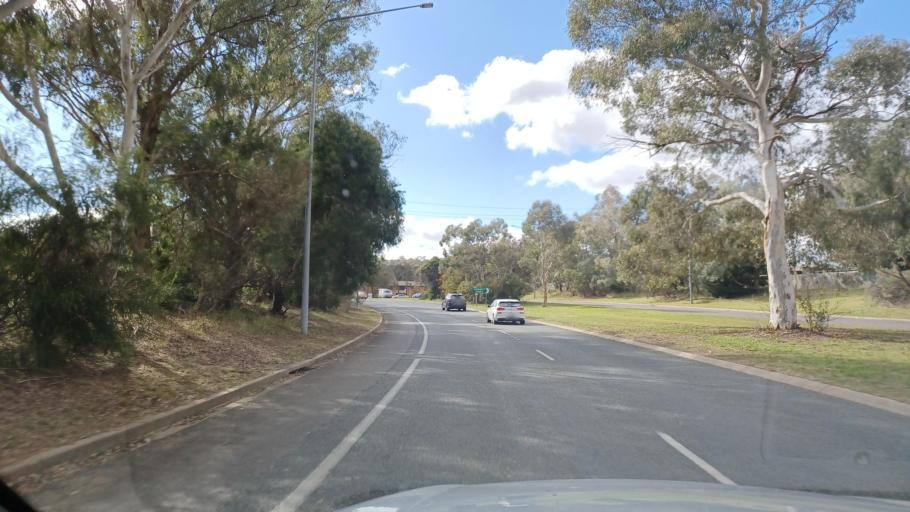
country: AU
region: Australian Capital Territory
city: Belconnen
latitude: -35.2119
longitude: 149.0477
